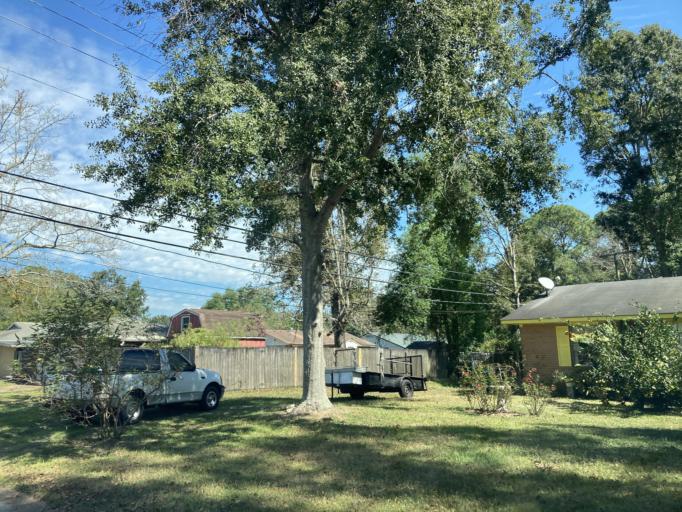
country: US
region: Mississippi
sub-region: Jackson County
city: Saint Martin
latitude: 30.4502
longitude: -88.8741
